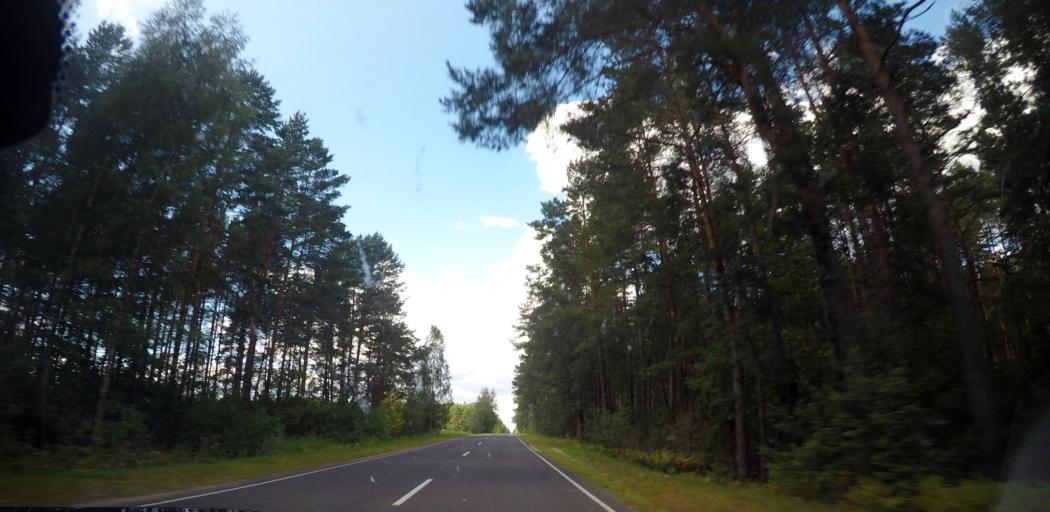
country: LT
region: Alytaus apskritis
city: Druskininkai
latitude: 53.8726
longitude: 24.1560
